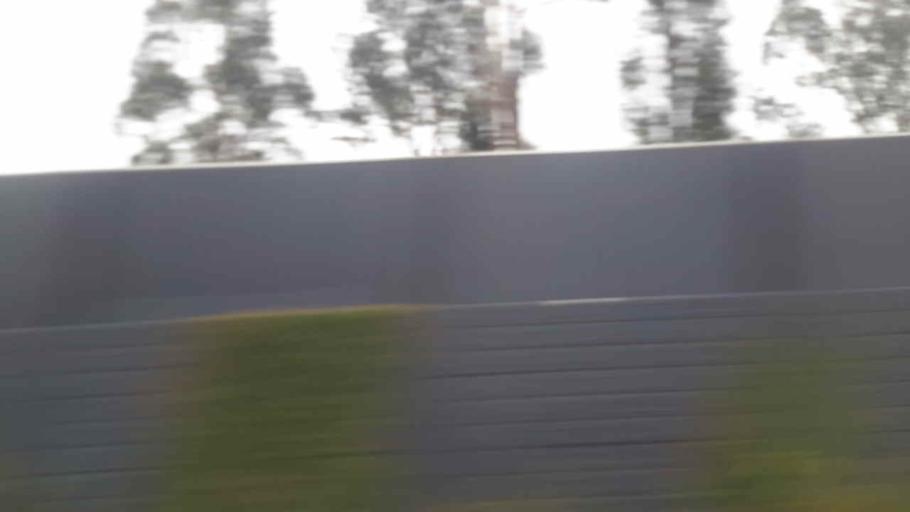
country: AU
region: New South Wales
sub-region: Penrith Municipality
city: Werrington Downs
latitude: -33.7277
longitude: 150.7201
